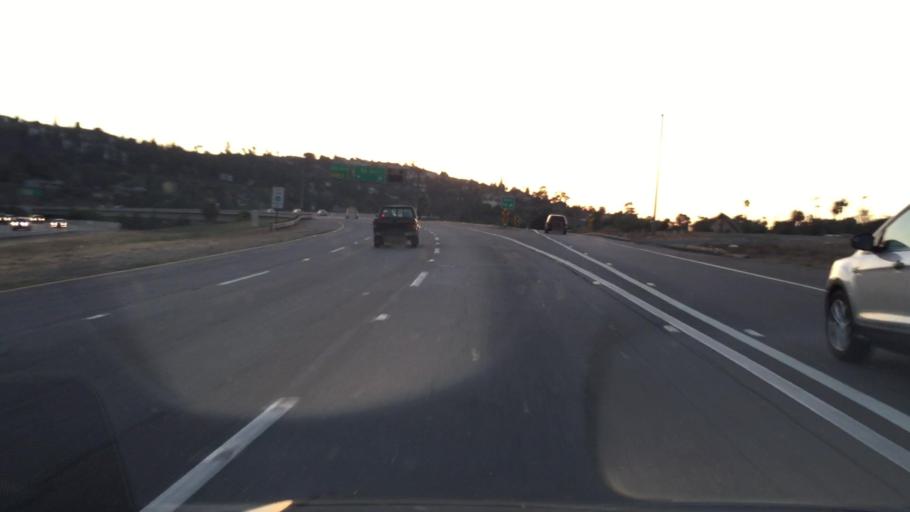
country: US
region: California
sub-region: San Diego County
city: Spring Valley
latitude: 32.7536
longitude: -117.0072
